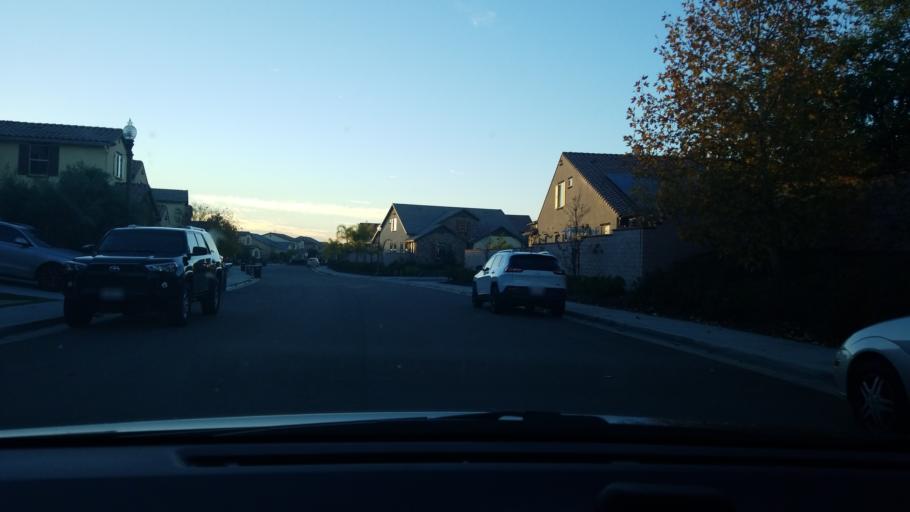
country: US
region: California
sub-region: Riverside County
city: Murrieta Hot Springs
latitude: 33.5512
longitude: -117.1058
